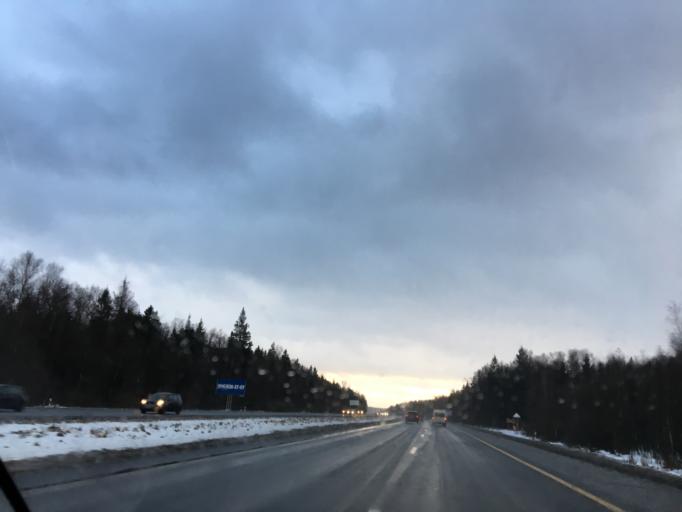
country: RU
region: Moskovskaya
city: Danki
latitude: 54.9702
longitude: 37.5296
